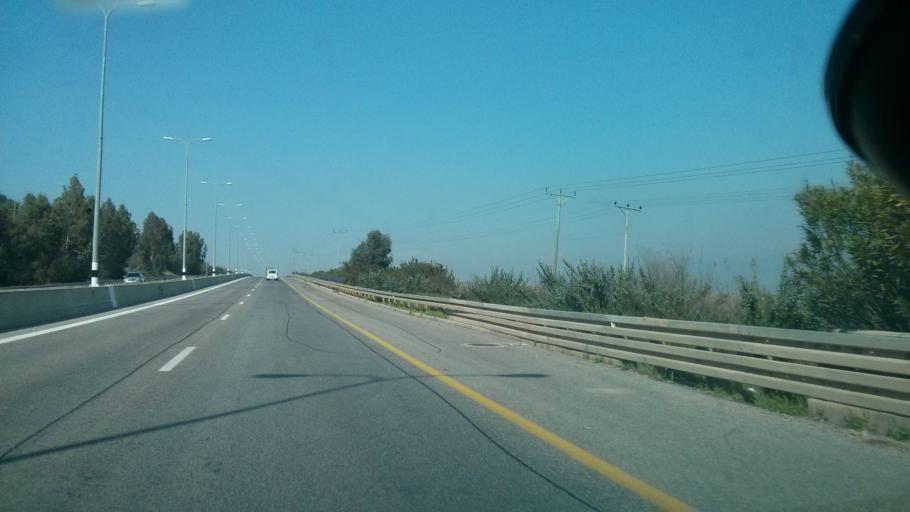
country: IL
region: Northern District
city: Rosh Pinna
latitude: 33.0843
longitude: 35.5750
